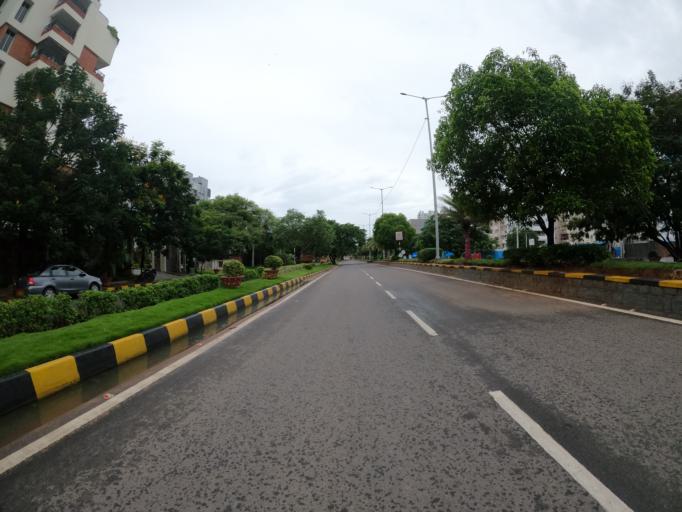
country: IN
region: Telangana
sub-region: Rangareddi
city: Kukatpalli
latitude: 17.4672
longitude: 78.3757
